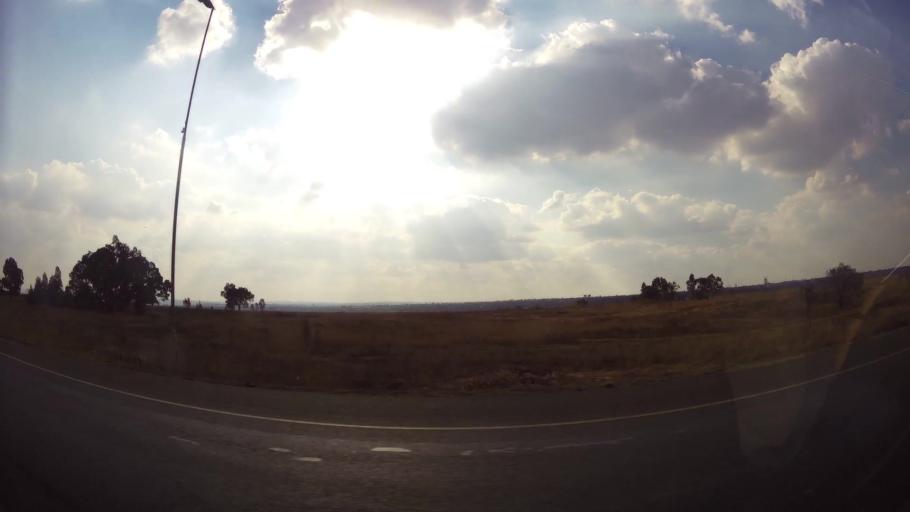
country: ZA
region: Gauteng
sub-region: Ekurhuleni Metropolitan Municipality
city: Boksburg
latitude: -26.2805
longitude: 28.2588
